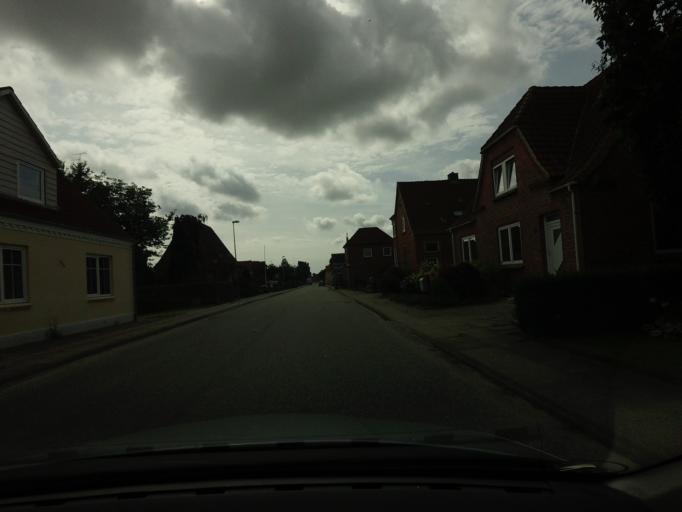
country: DK
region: North Denmark
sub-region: Bronderslev Kommune
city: Dronninglund
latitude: 57.2774
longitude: 10.3557
